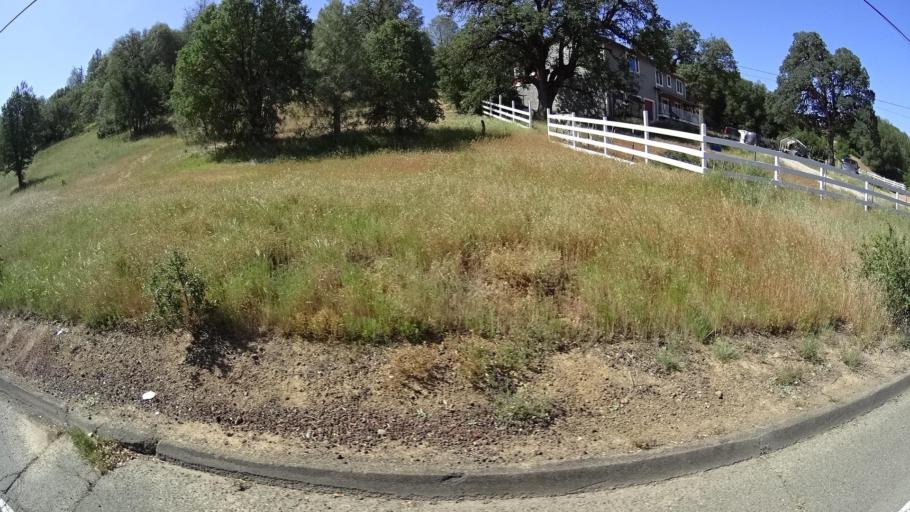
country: US
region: California
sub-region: Lake County
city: Lower Lake
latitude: 38.9087
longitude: -122.5823
